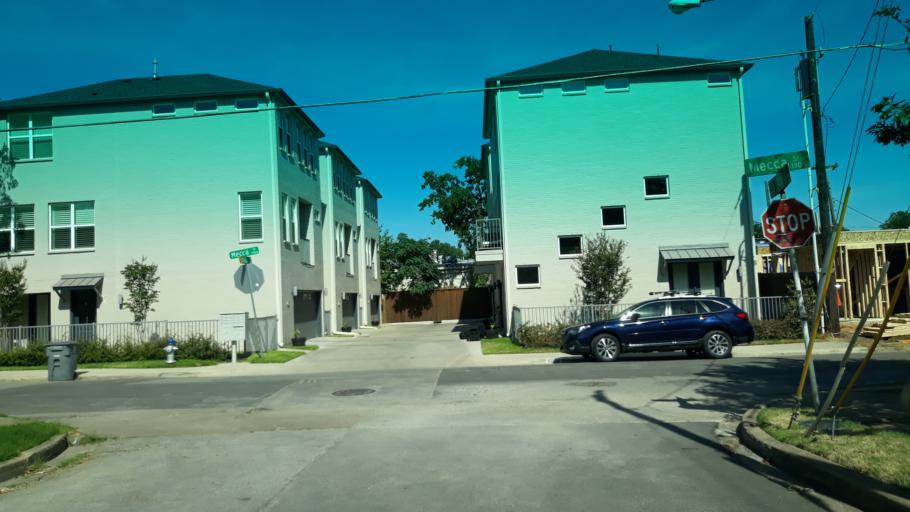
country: US
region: Texas
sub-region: Dallas County
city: Highland Park
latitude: 32.8130
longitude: -96.7629
